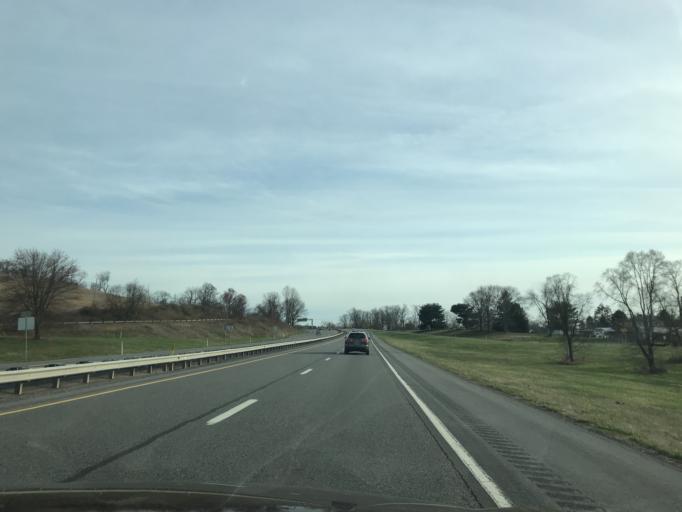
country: US
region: Pennsylvania
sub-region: Union County
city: New Columbia
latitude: 41.0486
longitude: -76.8406
